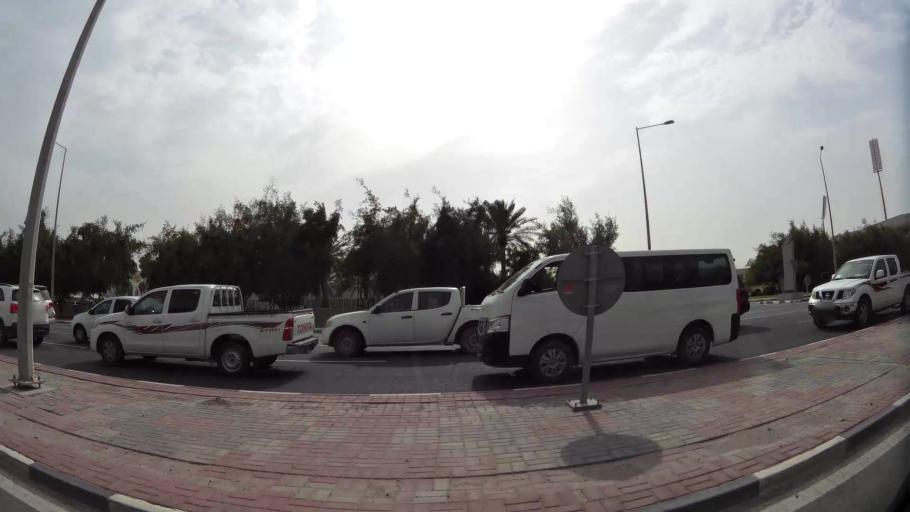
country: QA
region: Baladiyat ad Dawhah
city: Doha
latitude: 25.3157
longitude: 51.5151
